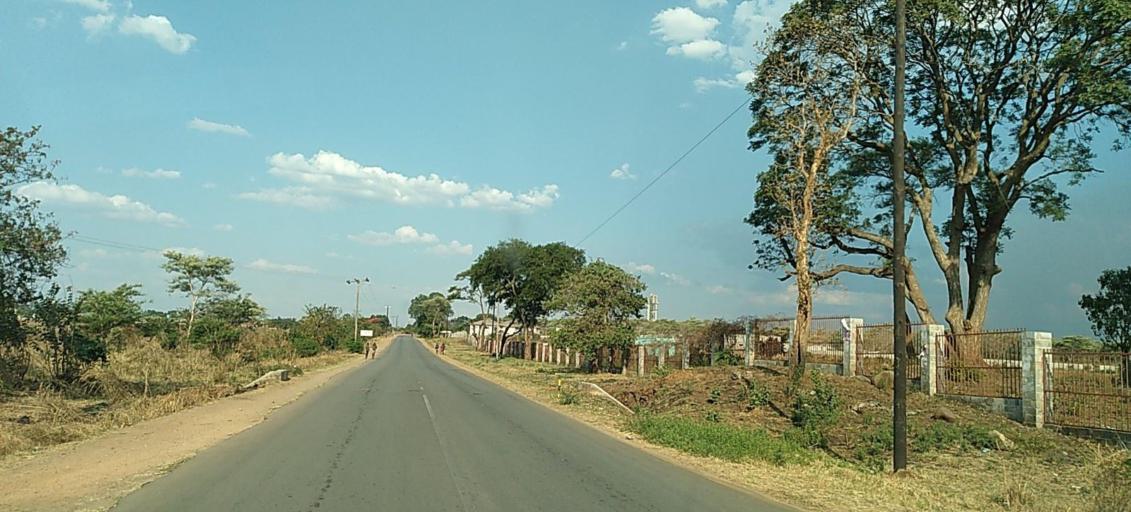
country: ZM
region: Lusaka
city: Lusaka
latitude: -15.5459
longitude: 28.2532
